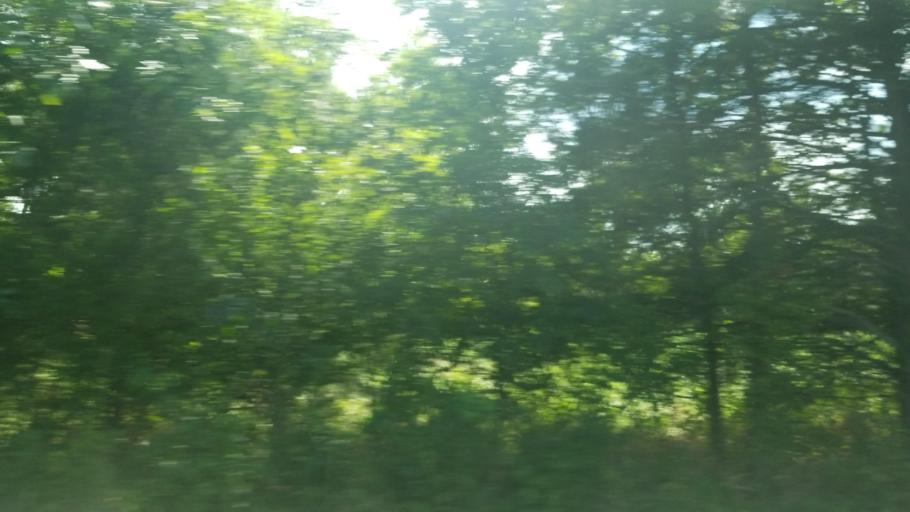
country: US
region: Illinois
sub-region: Saline County
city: Carrier Mills
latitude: 37.7919
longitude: -88.7595
